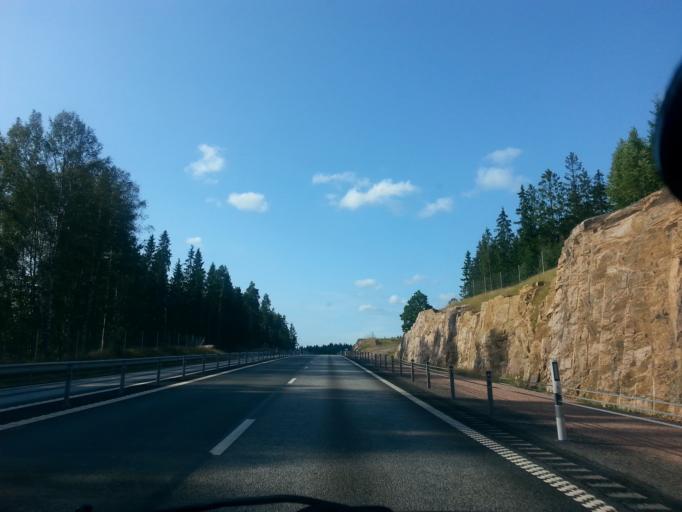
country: SE
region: Joenkoeping
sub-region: Gislaveds Kommun
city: Reftele
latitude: 57.2473
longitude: 13.6423
